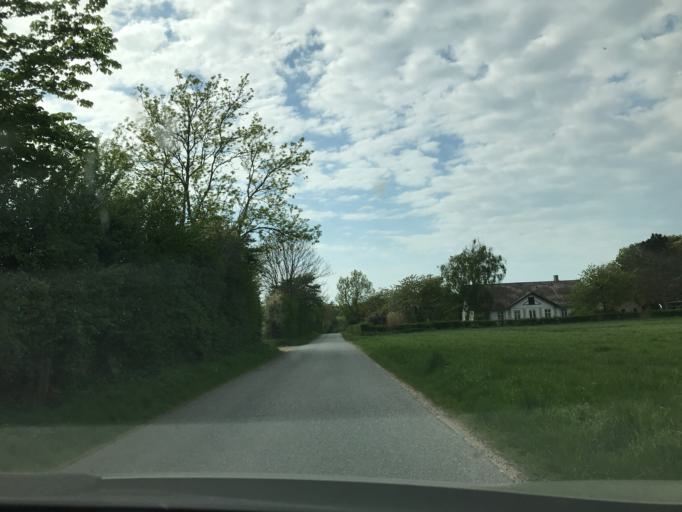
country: DK
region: South Denmark
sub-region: Middelfart Kommune
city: Norre Aby
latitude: 55.3640
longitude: 9.8420
